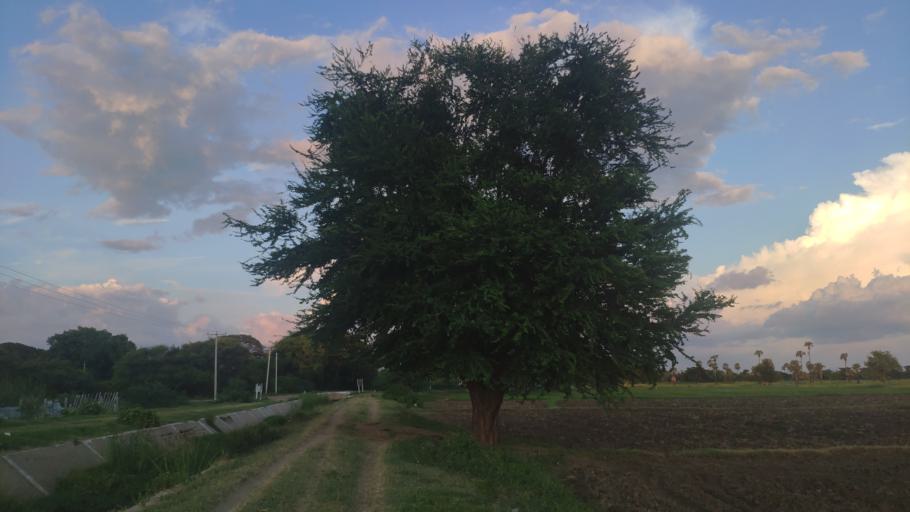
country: MM
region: Mandalay
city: Meiktila
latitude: 20.8679
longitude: 95.9293
